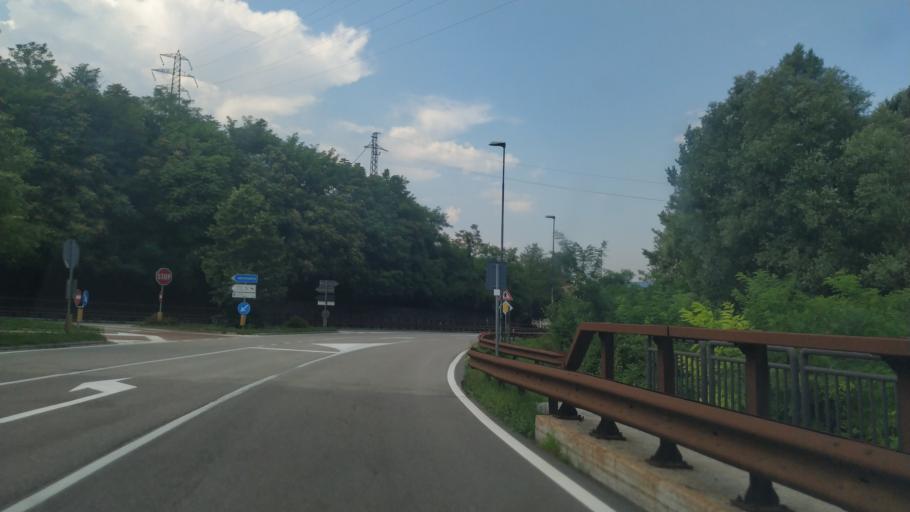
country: IT
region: Trentino-Alto Adige
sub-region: Provincia di Trento
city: Spormaggiore
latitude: 46.2383
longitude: 11.0559
